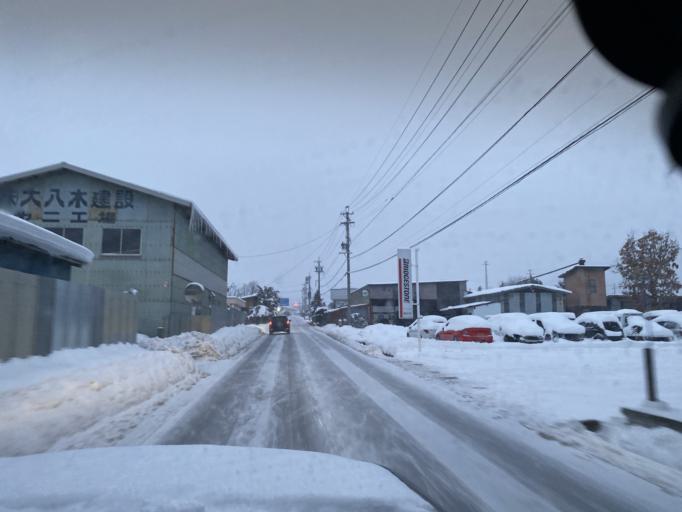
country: JP
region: Nagano
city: Omachi
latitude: 36.5230
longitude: 137.8370
